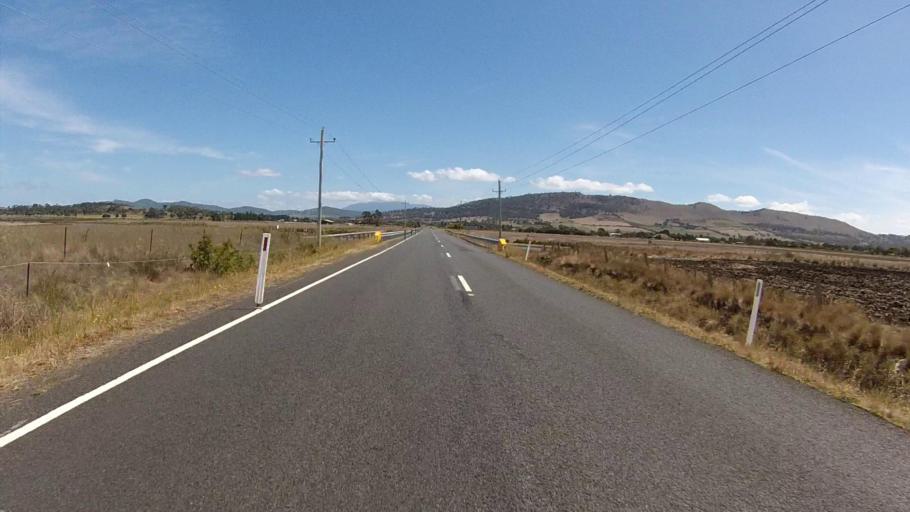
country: AU
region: Tasmania
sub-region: Sorell
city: Sorell
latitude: -42.7744
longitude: 147.5366
